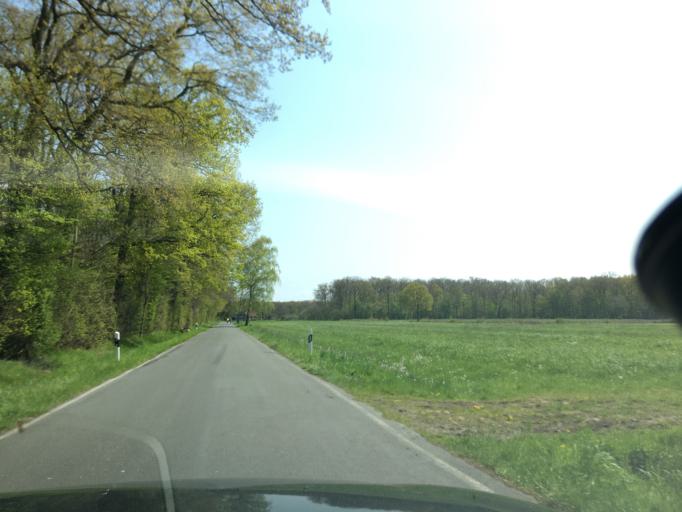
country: DE
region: North Rhine-Westphalia
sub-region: Regierungsbezirk Munster
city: Senden
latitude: 51.8526
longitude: 7.5377
